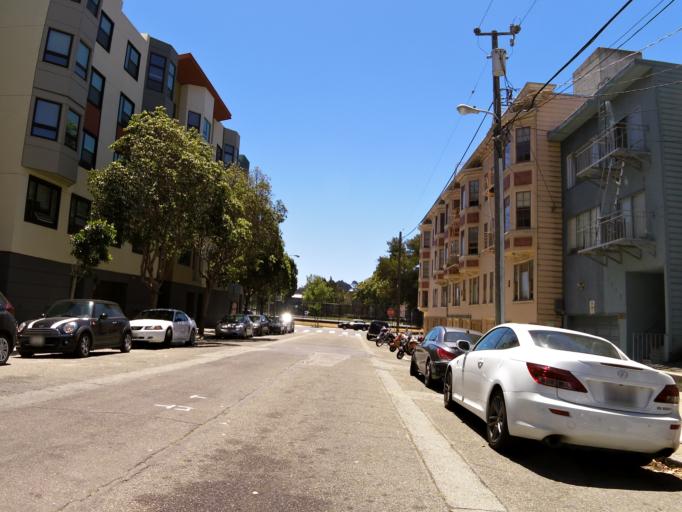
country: US
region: California
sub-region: San Francisco County
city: San Francisco
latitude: 37.7853
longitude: -122.4365
